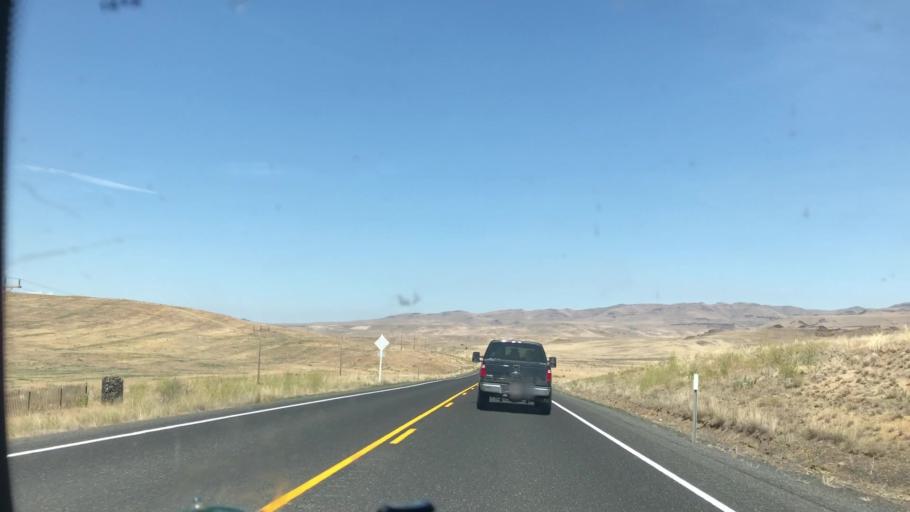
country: US
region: Idaho
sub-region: Owyhee County
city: Marsing
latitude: 43.2401
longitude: -117.0436
